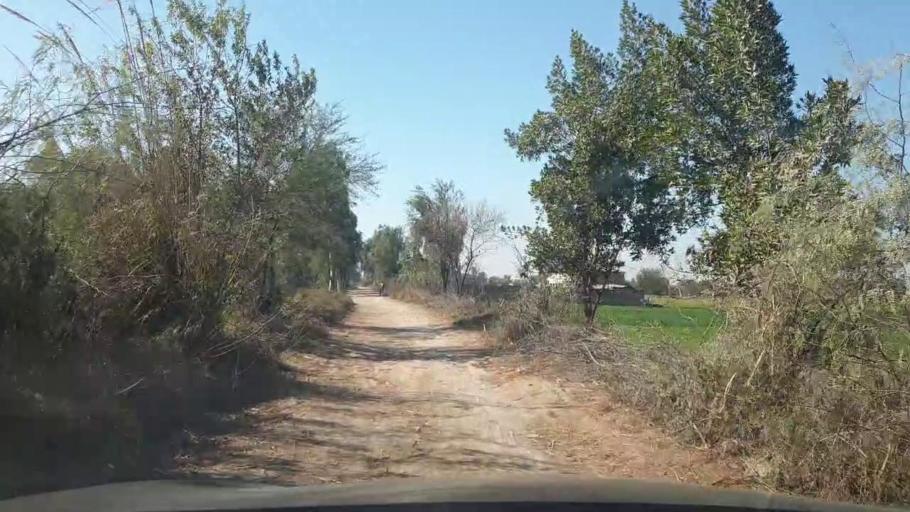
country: PK
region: Sindh
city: Mirpur Mathelo
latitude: 28.0613
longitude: 69.5019
